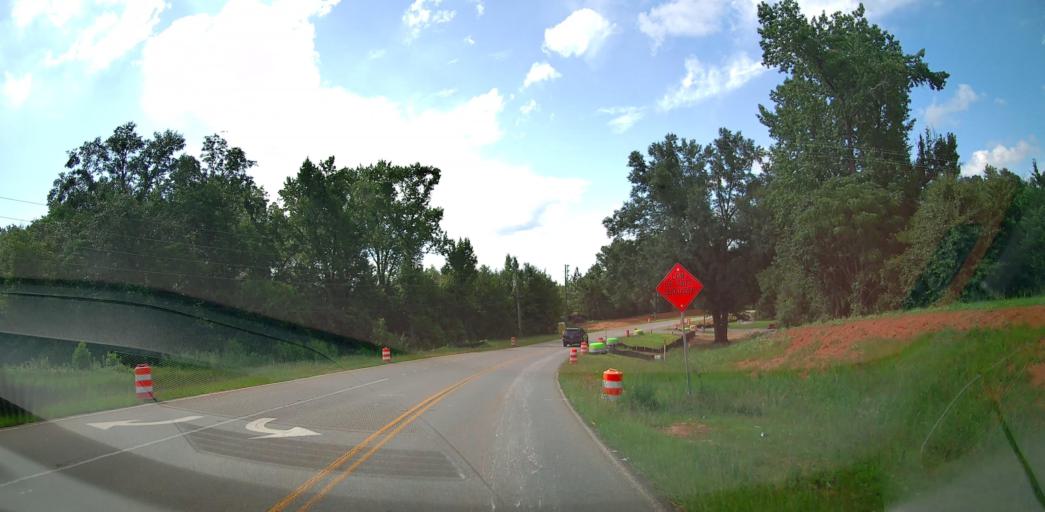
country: US
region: Georgia
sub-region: Houston County
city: Perry
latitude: 32.4777
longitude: -83.7027
